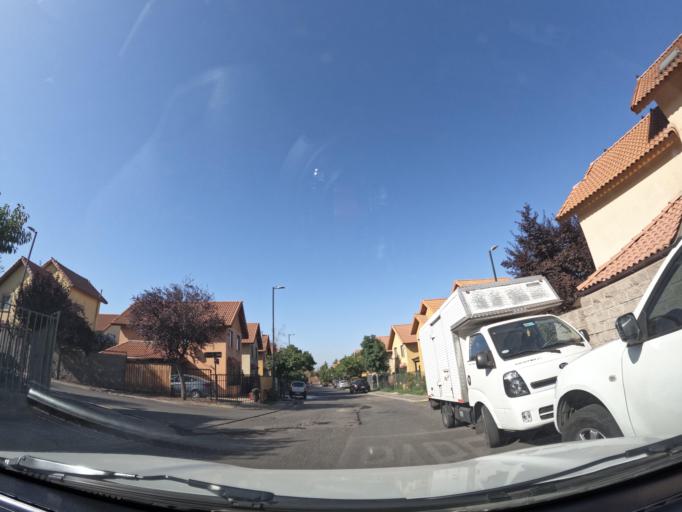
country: CL
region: Santiago Metropolitan
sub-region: Provincia de Santiago
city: Villa Presidente Frei, Nunoa, Santiago, Chile
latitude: -33.5104
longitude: -70.5469
